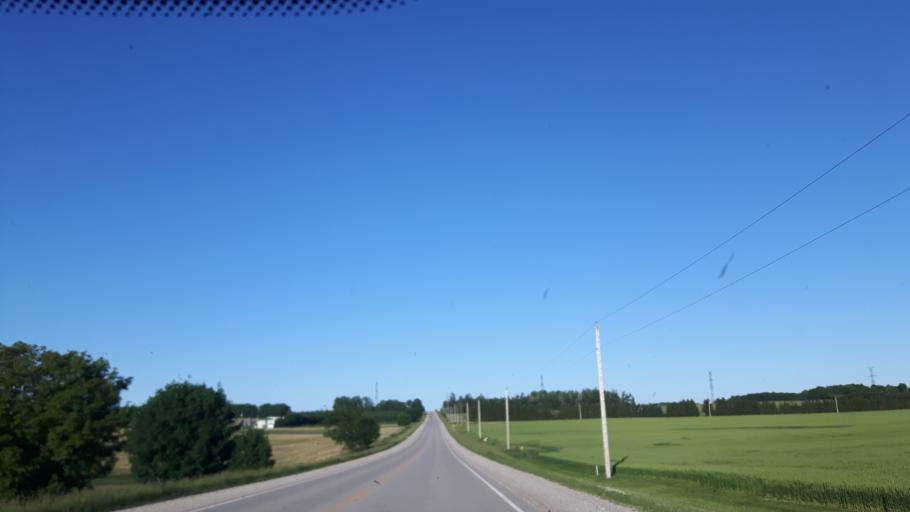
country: CA
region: Ontario
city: Goderich
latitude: 43.6427
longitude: -81.6494
